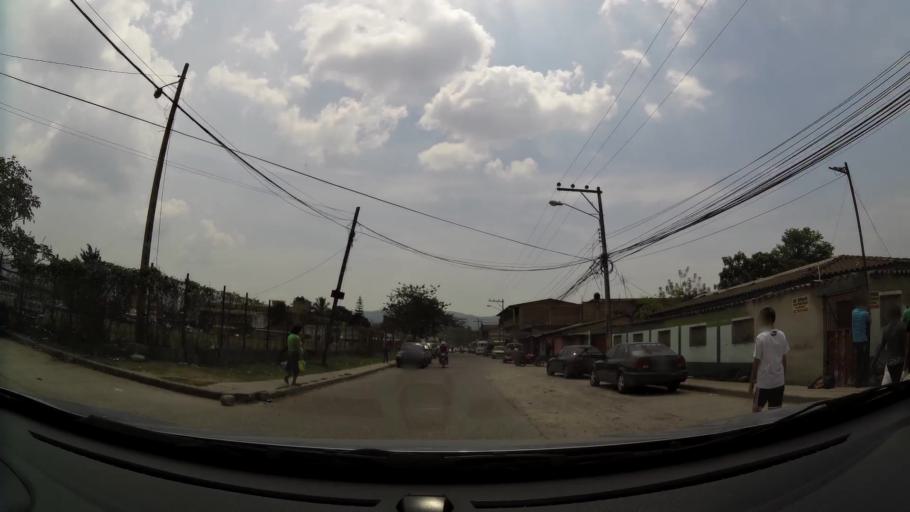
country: HN
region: Comayagua
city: Siguatepeque
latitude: 14.5894
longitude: -87.8359
